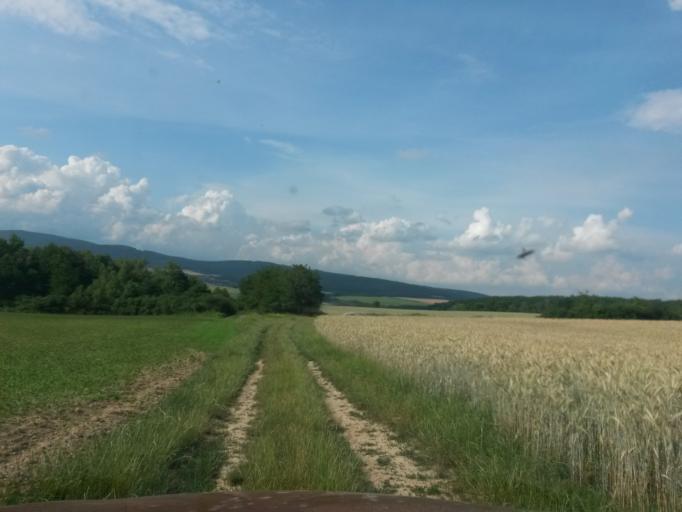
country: SK
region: Kosicky
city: Moldava nad Bodvou
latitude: 48.6445
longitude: 21.1093
